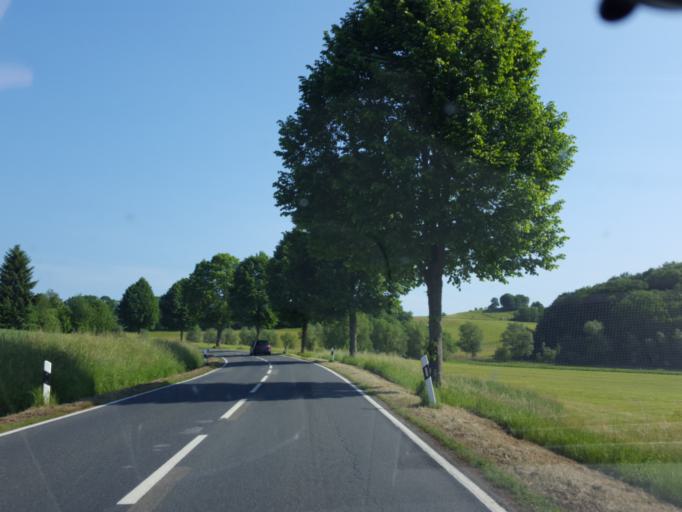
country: DE
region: Lower Saxony
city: Osterode am Harz
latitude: 51.6919
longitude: 10.2469
